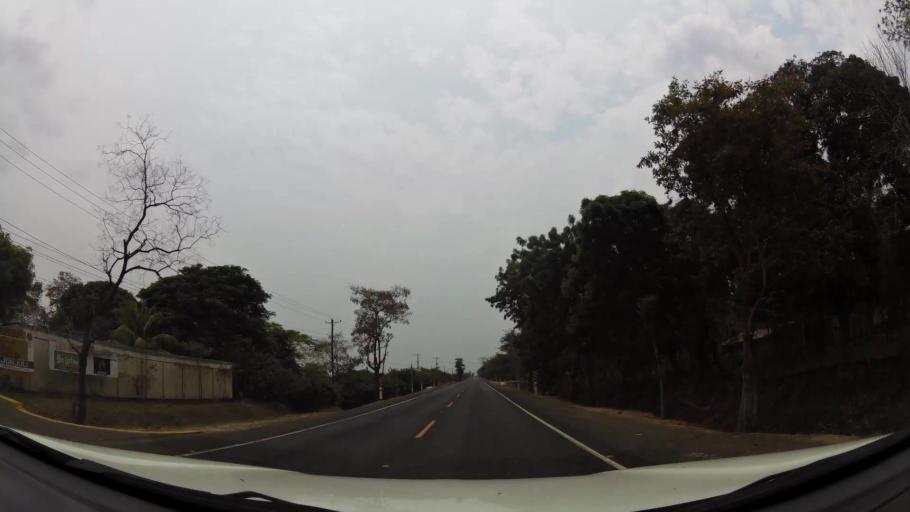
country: NI
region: Leon
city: Quezalguaque
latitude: 12.5408
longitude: -86.9131
